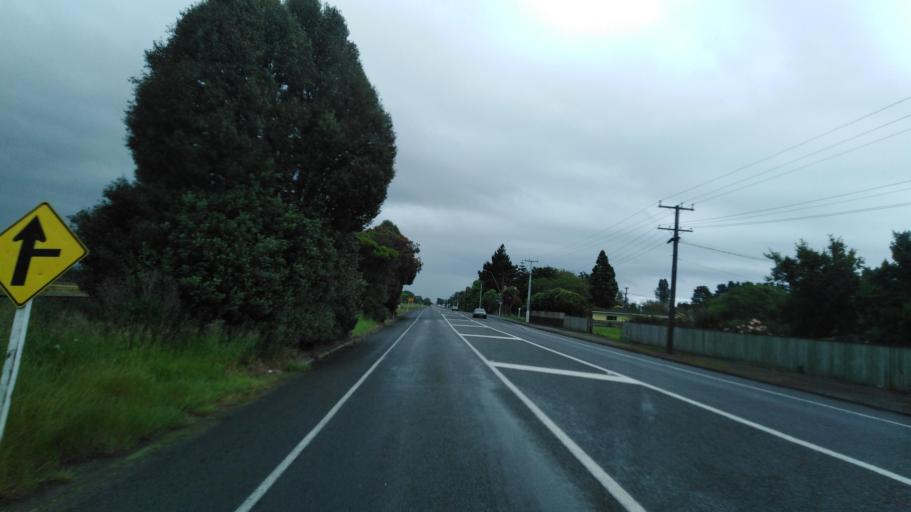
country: NZ
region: Manawatu-Wanganui
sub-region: Horowhenua District
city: Levin
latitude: -40.6417
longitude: 175.2670
